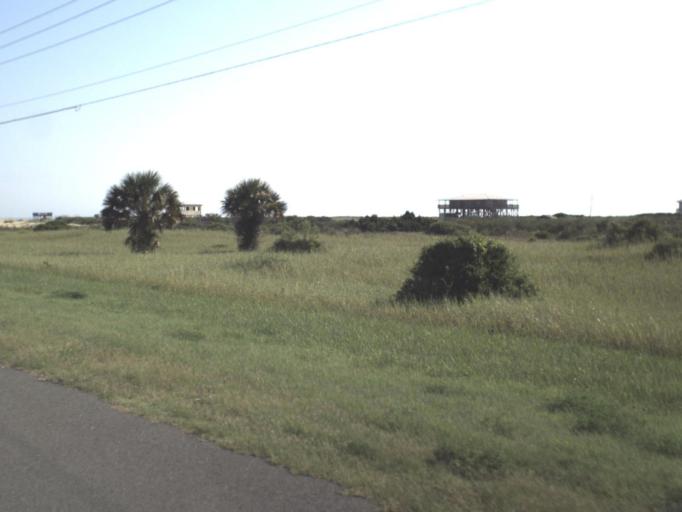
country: US
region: Florida
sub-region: Flagler County
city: Palm Coast
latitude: 29.6870
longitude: -81.2228
